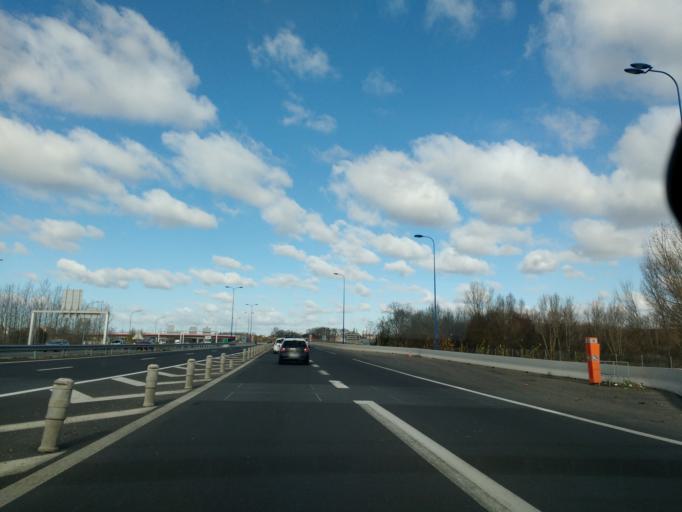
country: FR
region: Midi-Pyrenees
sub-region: Departement de la Haute-Garonne
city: Ramonville-Saint-Agne
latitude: 43.5600
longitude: 1.4897
